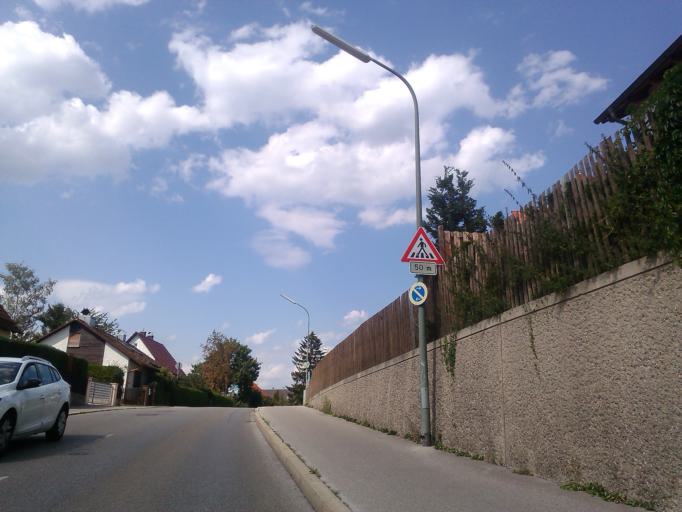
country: DE
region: Bavaria
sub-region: Upper Bavaria
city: Germering
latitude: 48.1268
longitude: 11.3546
